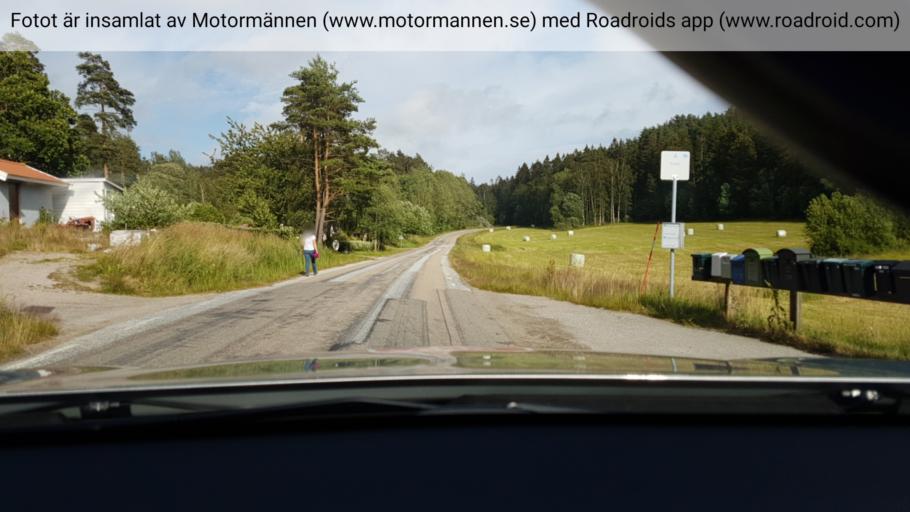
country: SE
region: Vaestra Goetaland
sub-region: Tjorns Kommun
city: Myggenas
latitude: 58.1281
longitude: 11.6667
